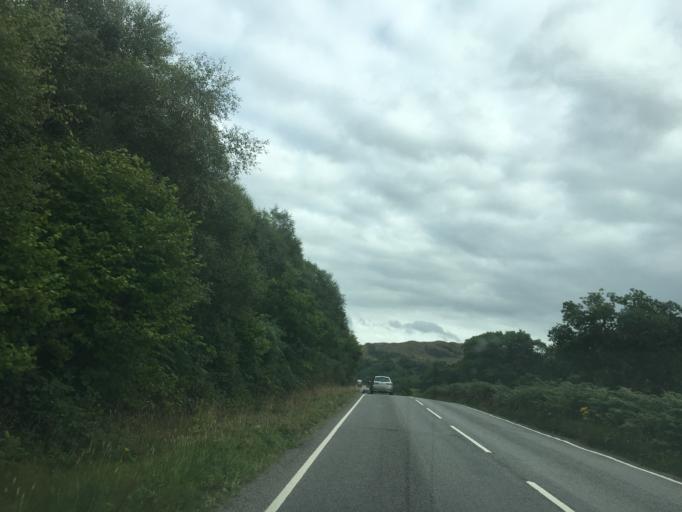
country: GB
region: Scotland
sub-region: Argyll and Bute
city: Oban
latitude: 56.3260
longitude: -5.5016
